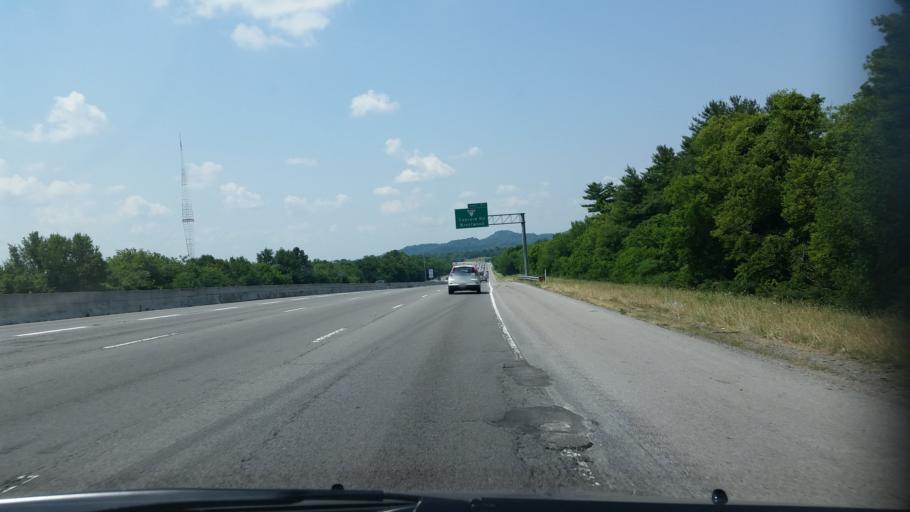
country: US
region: Tennessee
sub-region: Williamson County
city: Brentwood Estates
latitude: 36.0088
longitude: -86.7866
